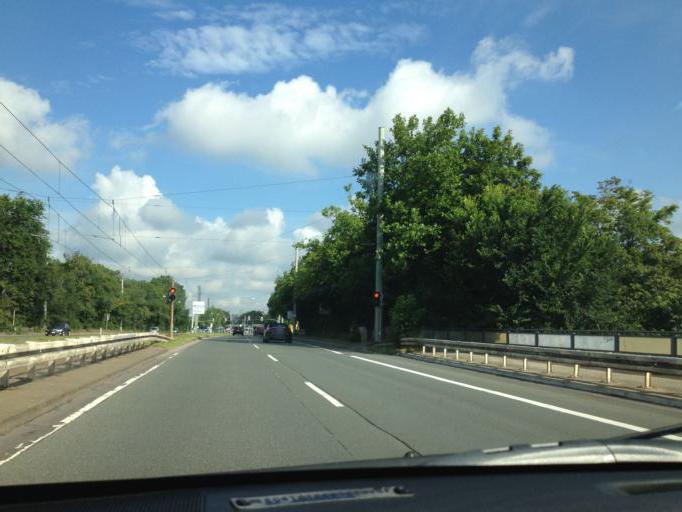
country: DE
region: North Rhine-Westphalia
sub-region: Regierungsbezirk Arnsberg
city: Bochum
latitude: 51.4667
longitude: 7.2727
